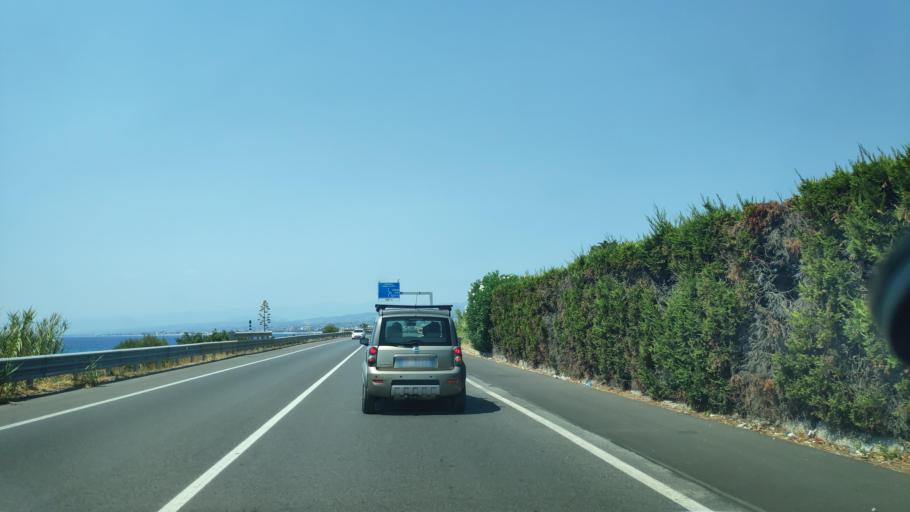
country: IT
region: Calabria
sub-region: Provincia di Reggio Calabria
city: Marina di Gioiosa Ionica
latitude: 38.3065
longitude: 16.3580
